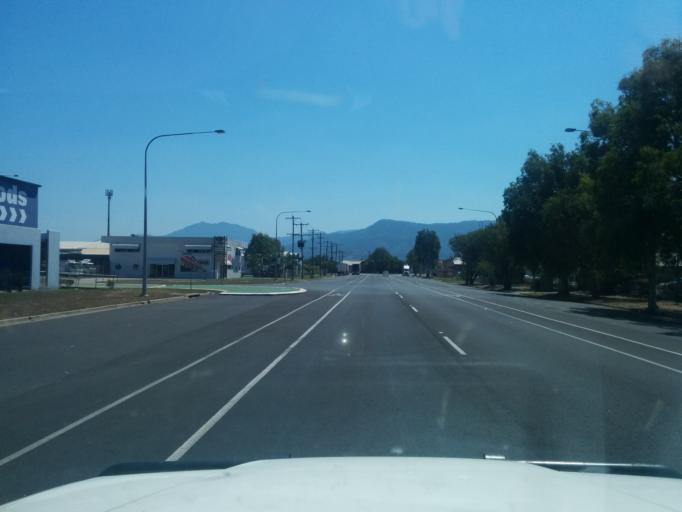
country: AU
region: Queensland
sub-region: Cairns
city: Cairns
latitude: -16.9415
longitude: 145.7727
